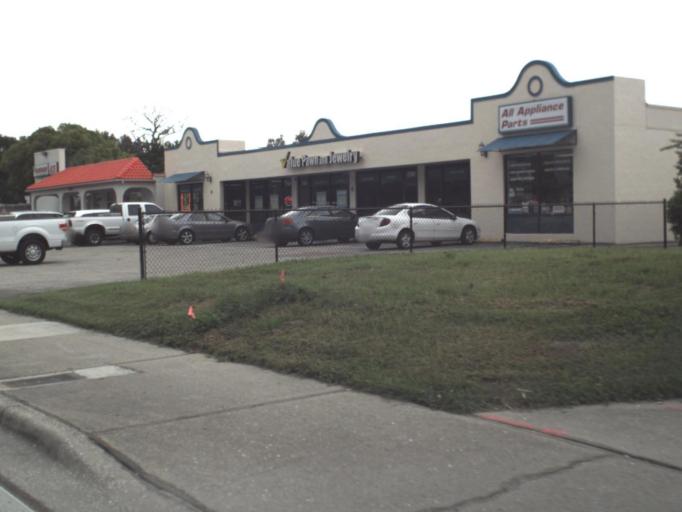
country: US
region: Florida
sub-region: Sarasota County
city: Southgate
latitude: 27.2987
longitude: -82.5077
